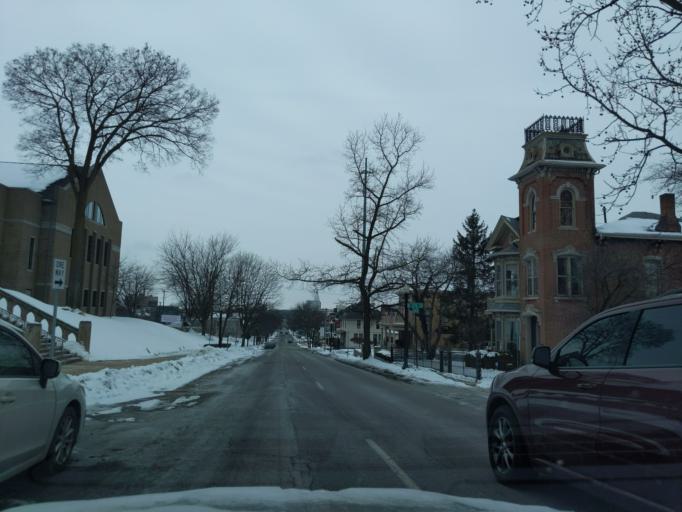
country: US
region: Indiana
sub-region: Tippecanoe County
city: Lafayette
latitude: 40.4183
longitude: -86.8836
